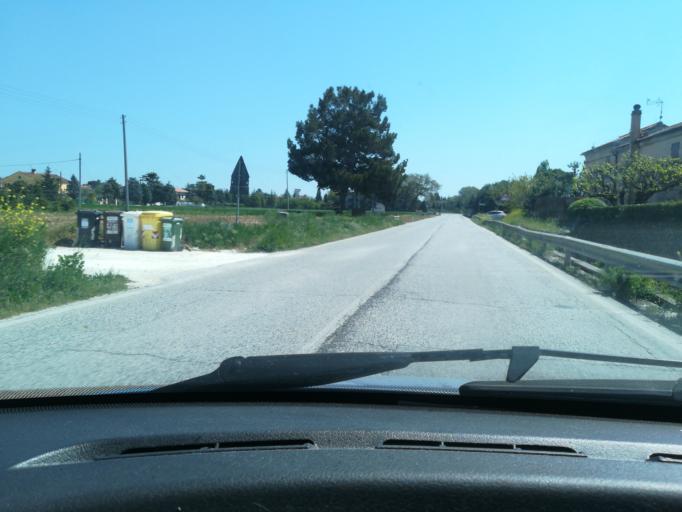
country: IT
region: The Marches
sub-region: Provincia di Ancona
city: Castelfidardo
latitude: 43.4531
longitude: 13.5278
